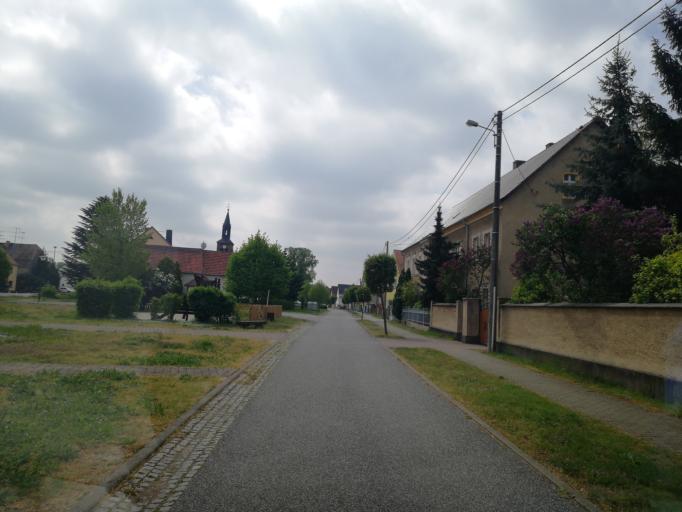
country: DE
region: Saxony
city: Beilrode
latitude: 51.6422
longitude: 13.1194
